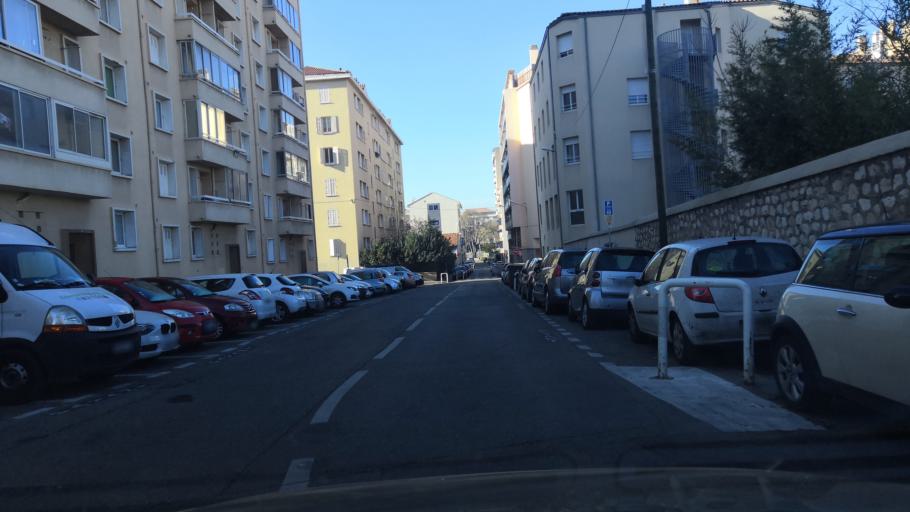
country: FR
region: Provence-Alpes-Cote d'Azur
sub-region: Departement des Bouches-du-Rhone
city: Marseille 05
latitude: 43.2967
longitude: 5.4030
